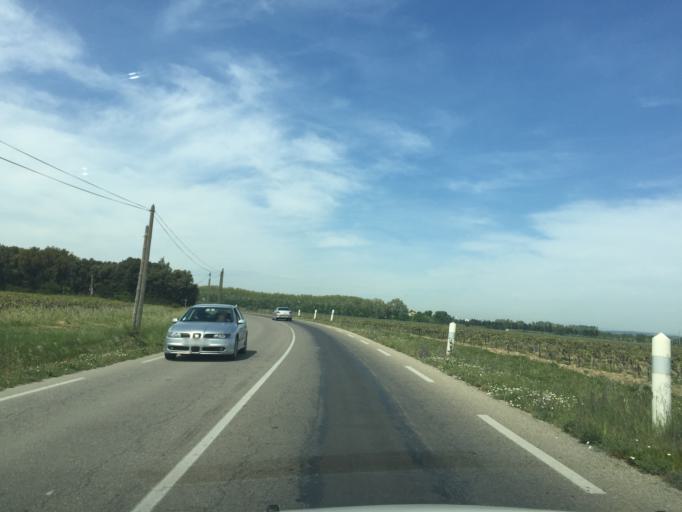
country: FR
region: Provence-Alpes-Cote d'Azur
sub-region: Departement du Vaucluse
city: Jonquieres
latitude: 44.1180
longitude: 4.8723
